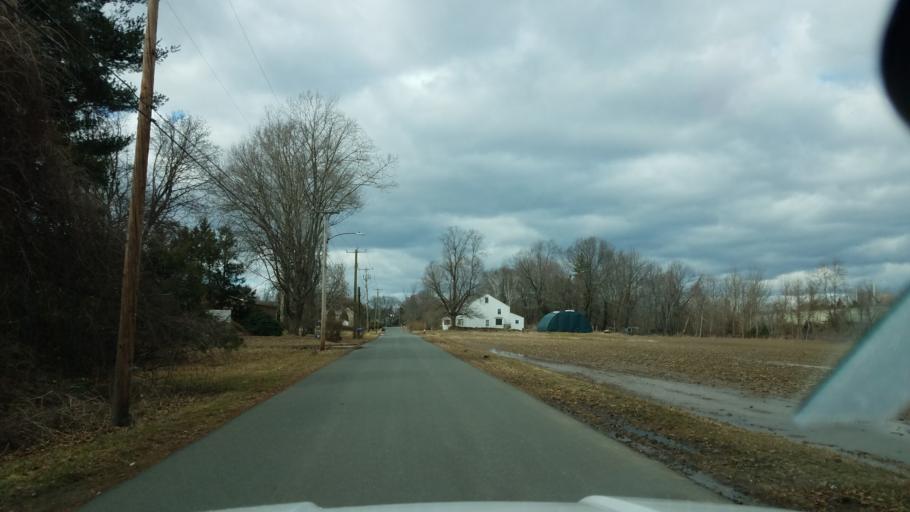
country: US
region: Connecticut
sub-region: Hartford County
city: Wethersfield
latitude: 41.7014
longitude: -72.6471
